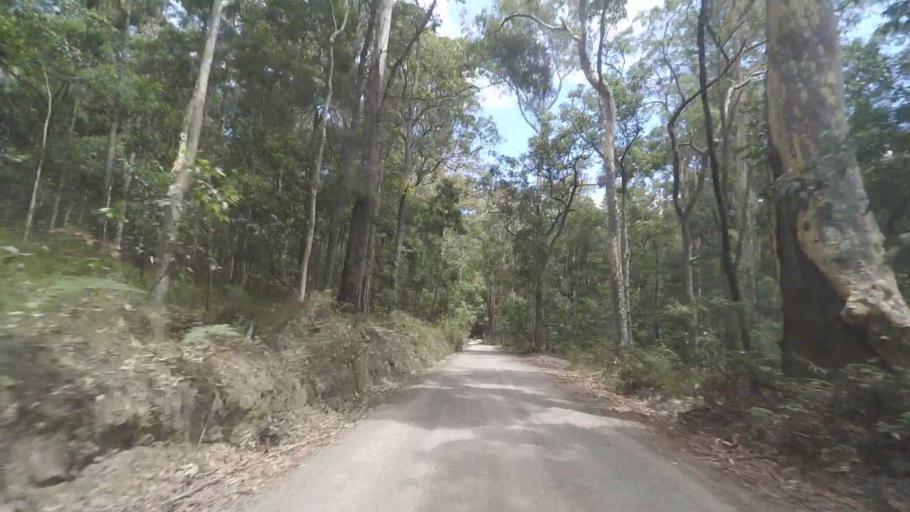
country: AU
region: New South Wales
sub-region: Shoalhaven Shire
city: Milton
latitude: -35.4402
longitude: 150.3165
